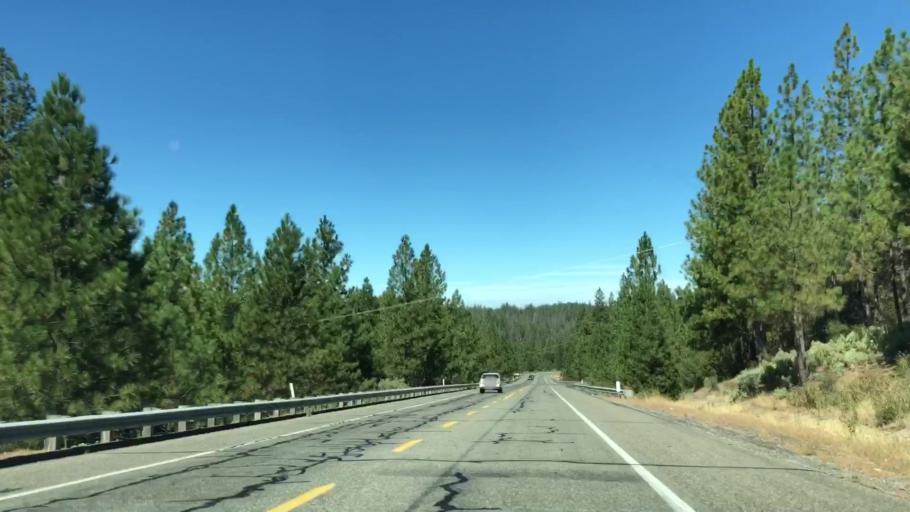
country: US
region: California
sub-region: Tuolumne County
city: Tuolumne City
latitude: 37.8314
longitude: -120.1990
